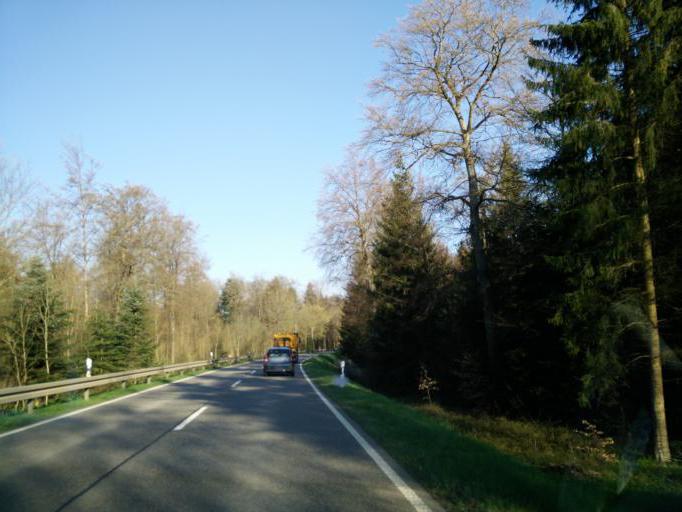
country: DE
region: Baden-Wuerttemberg
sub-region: Karlsruhe Region
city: Althengstett
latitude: 48.6760
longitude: 8.7799
